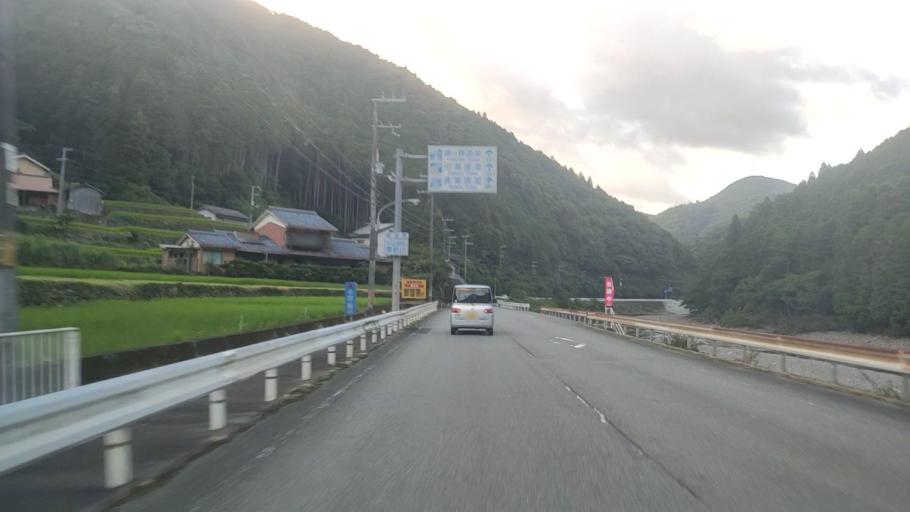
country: JP
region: Wakayama
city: Tanabe
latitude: 33.7838
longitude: 135.5054
